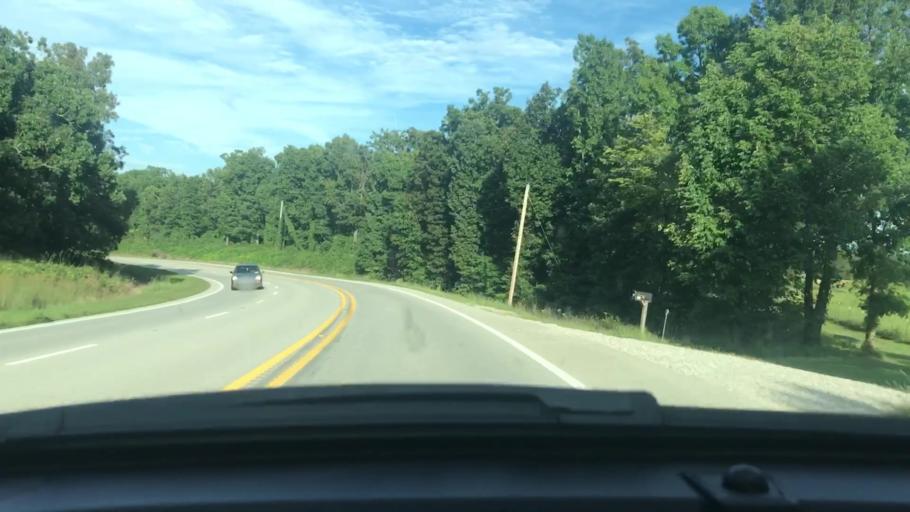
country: US
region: Arkansas
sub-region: Sharp County
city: Cherokee Village
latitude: 36.2716
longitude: -91.3688
